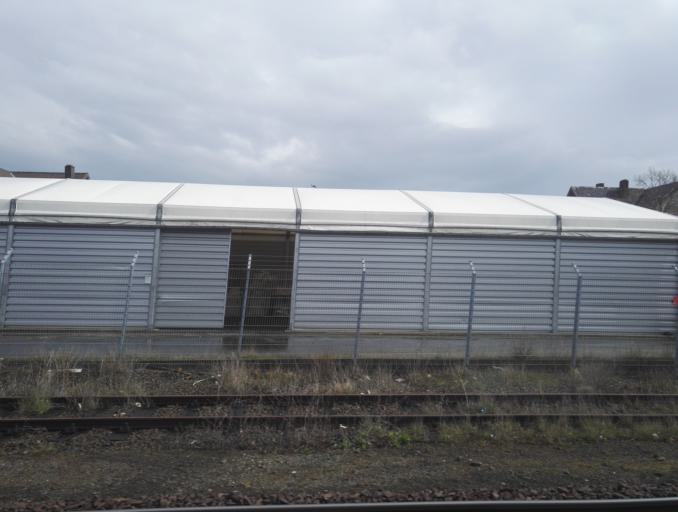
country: DE
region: Lower Saxony
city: Goslar
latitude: 51.9057
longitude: 10.4771
